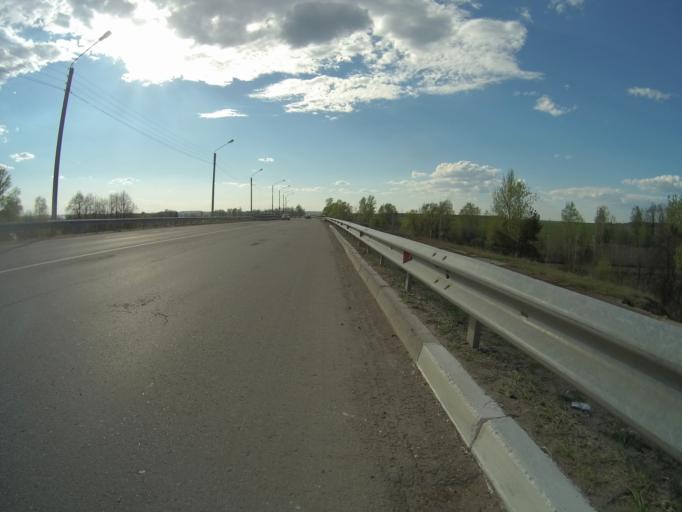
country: RU
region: Vladimir
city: Orgtrud
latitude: 56.2106
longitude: 40.5891
